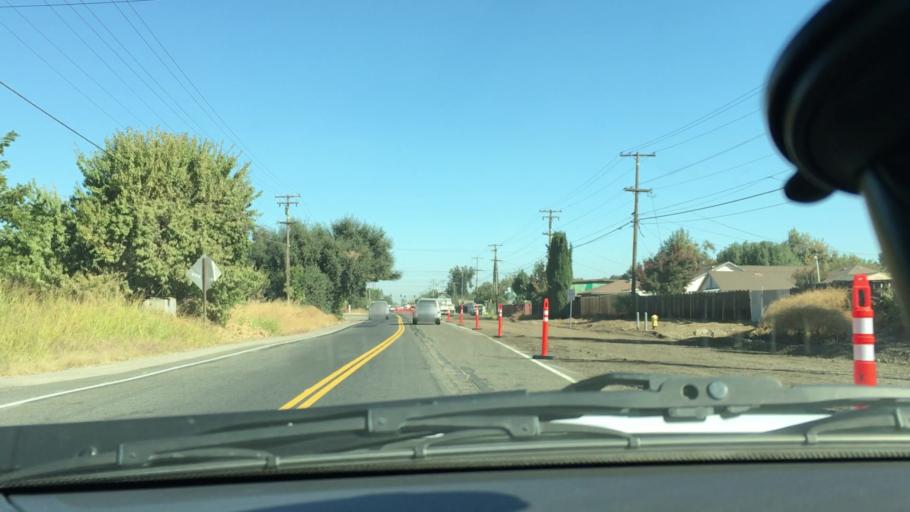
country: US
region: California
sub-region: Stanislaus County
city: West Modesto
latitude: 37.6178
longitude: -121.0304
